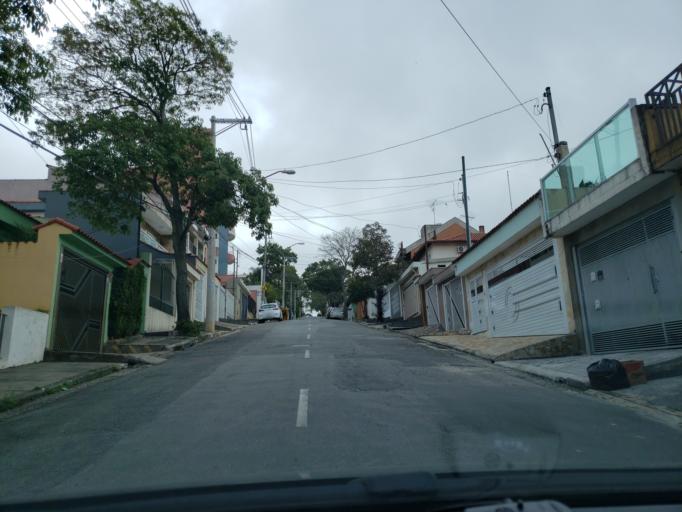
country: BR
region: Sao Paulo
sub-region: Sao Bernardo Do Campo
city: Sao Bernardo do Campo
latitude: -23.6744
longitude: -46.5663
